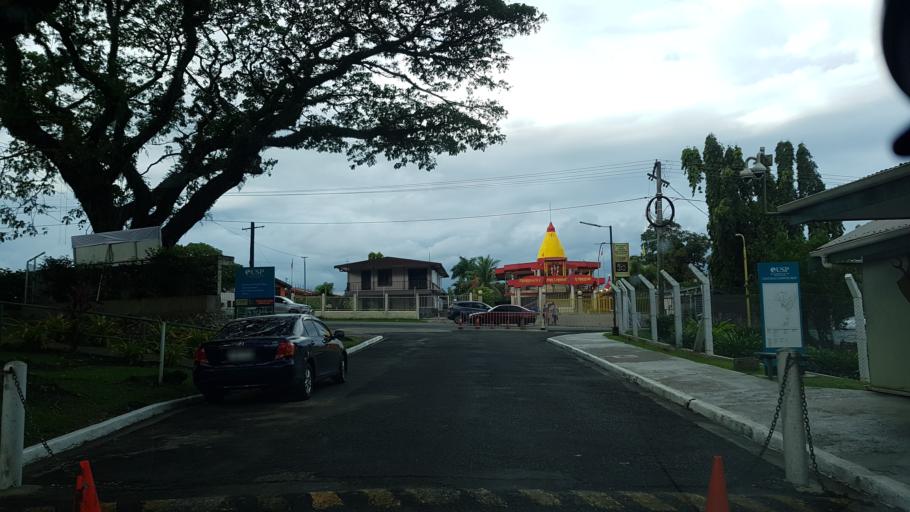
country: FJ
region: Central
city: Suva
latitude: -18.1470
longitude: 178.4449
